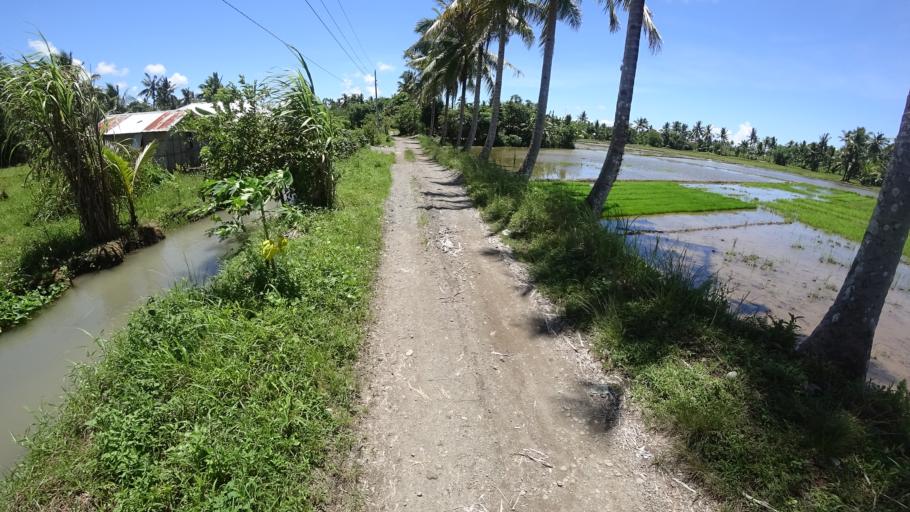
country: PH
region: Eastern Visayas
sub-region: Province of Leyte
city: MacArthur
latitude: 10.8504
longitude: 124.9659
